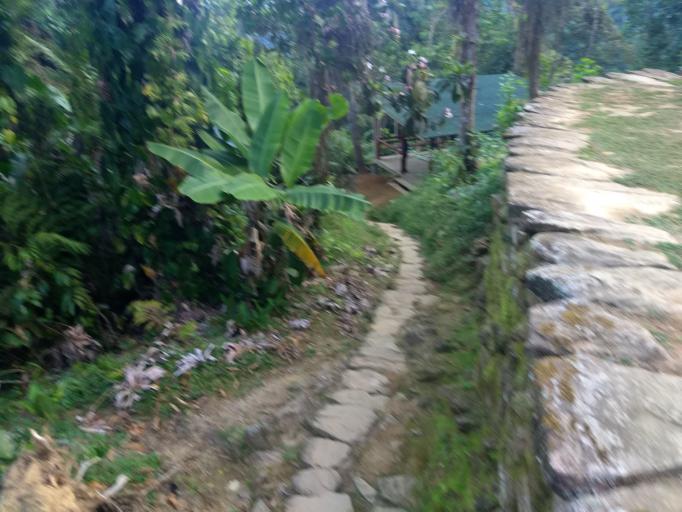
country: CO
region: Magdalena
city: Cienaga
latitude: 11.0424
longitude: -73.9243
